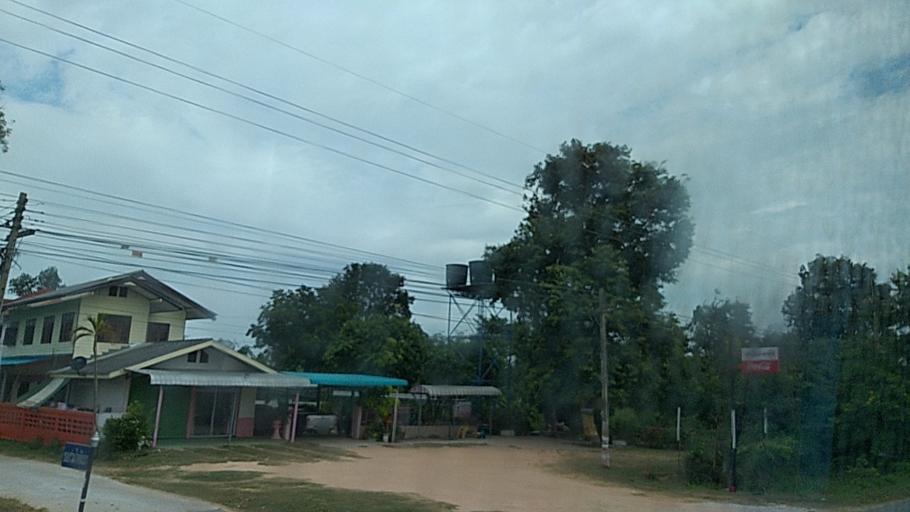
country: TH
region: Roi Et
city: Changhan
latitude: 16.1095
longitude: 103.5085
